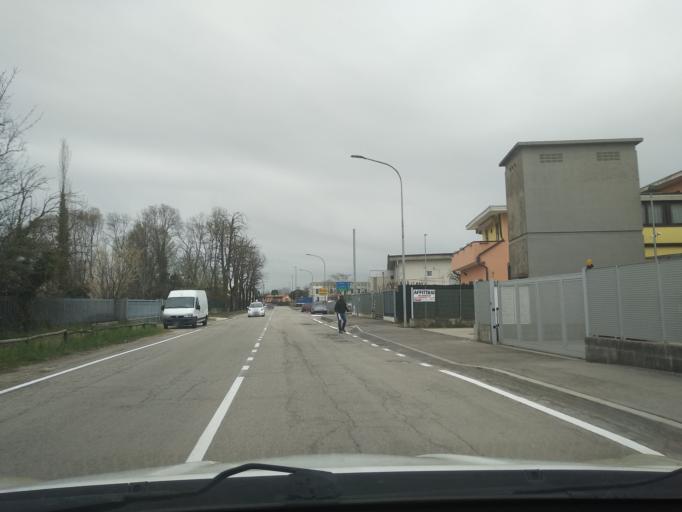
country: IT
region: Veneto
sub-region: Provincia di Padova
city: Rubano
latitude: 45.4242
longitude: 11.7916
